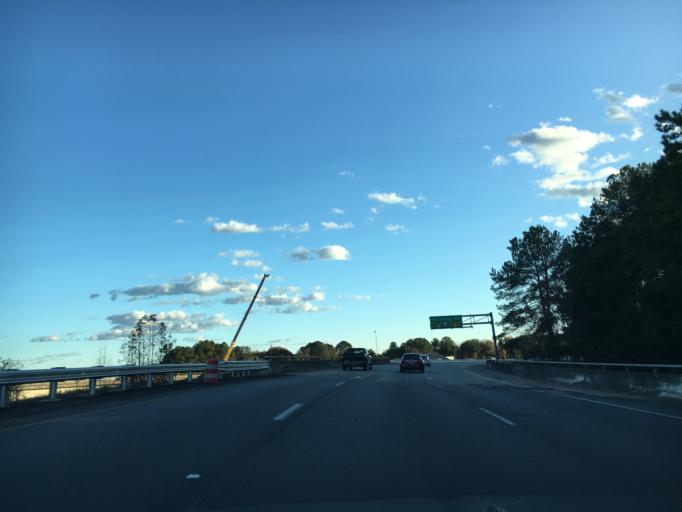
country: US
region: South Carolina
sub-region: Richland County
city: Dentsville
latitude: 34.0943
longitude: -80.9563
